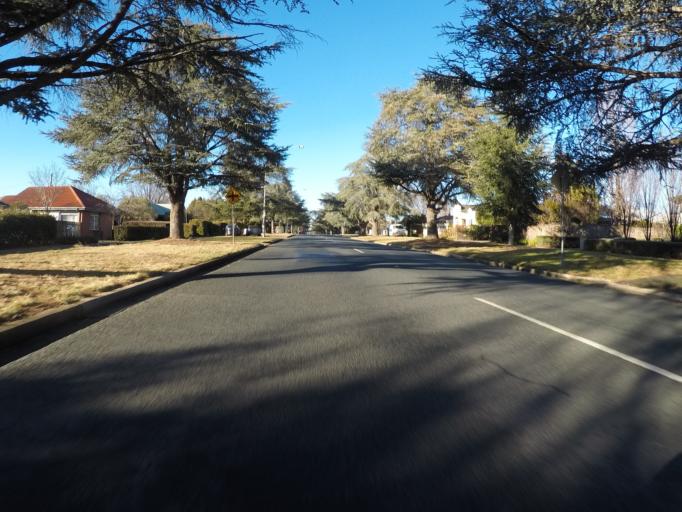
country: AU
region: Australian Capital Territory
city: Forrest
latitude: -35.3087
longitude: 149.0983
